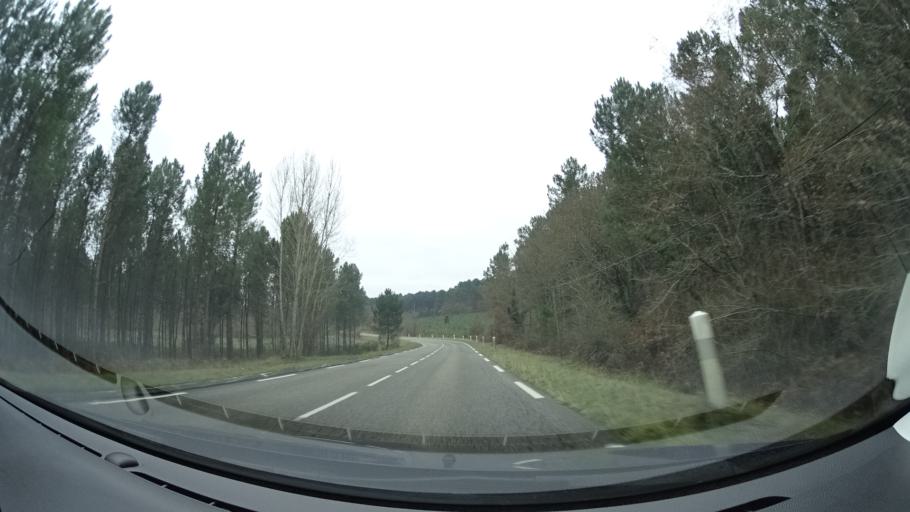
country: FR
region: Aquitaine
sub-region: Departement du Lot-et-Garonne
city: Damazan
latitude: 44.2610
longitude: 0.2371
